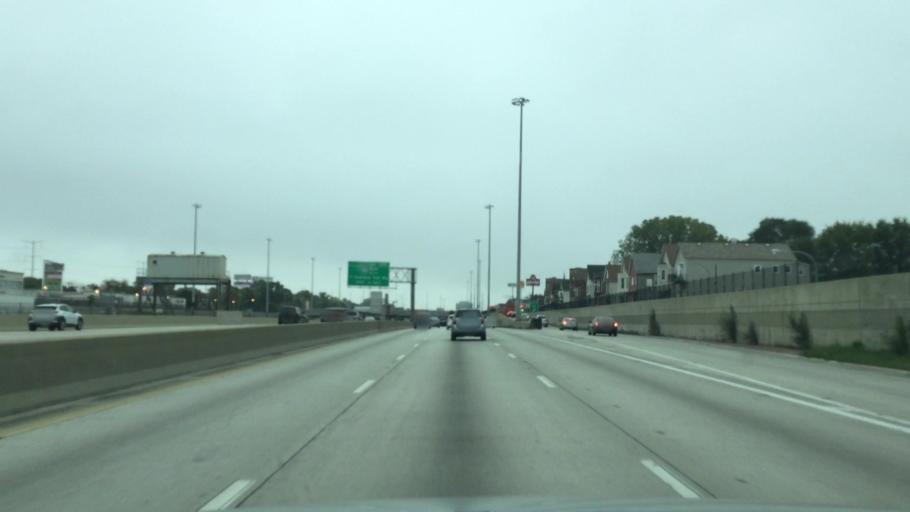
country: US
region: Illinois
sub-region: Cook County
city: Chicago
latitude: 41.7986
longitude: -87.6317
